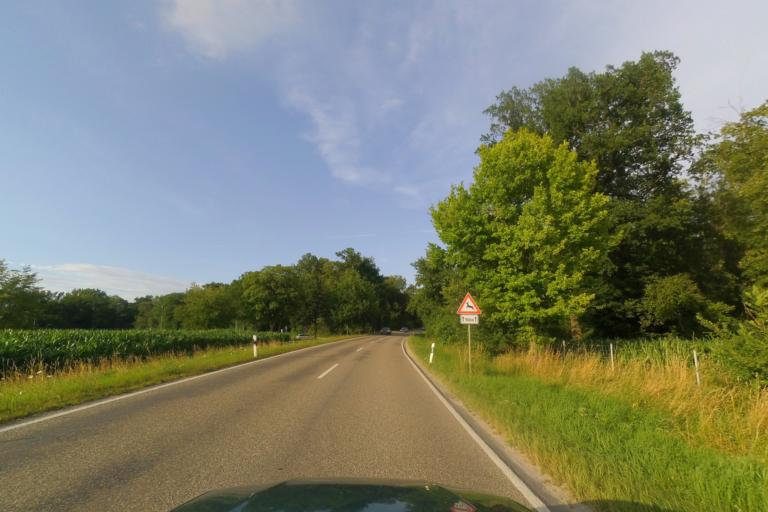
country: DE
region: Bavaria
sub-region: Swabia
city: Lauingen
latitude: 48.5664
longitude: 10.4464
